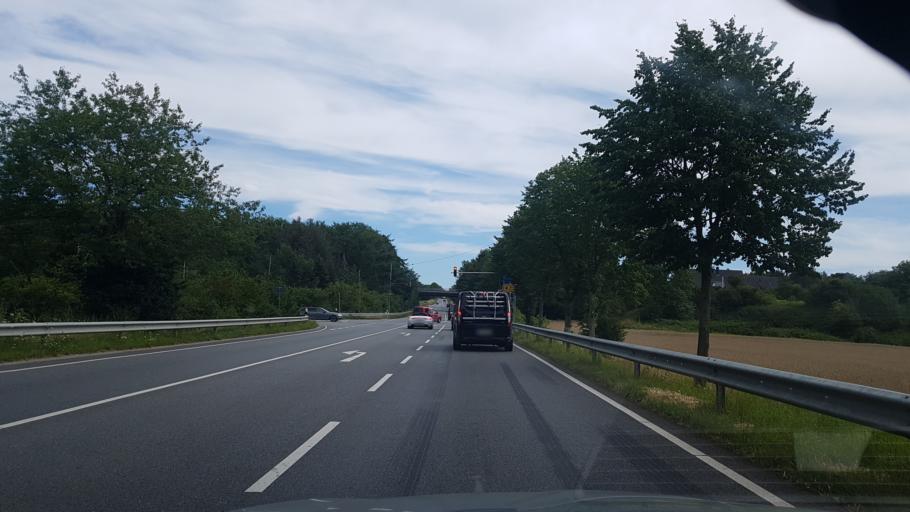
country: DE
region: Schleswig-Holstein
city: Bordesholm
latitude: 54.1872
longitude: 10.0213
